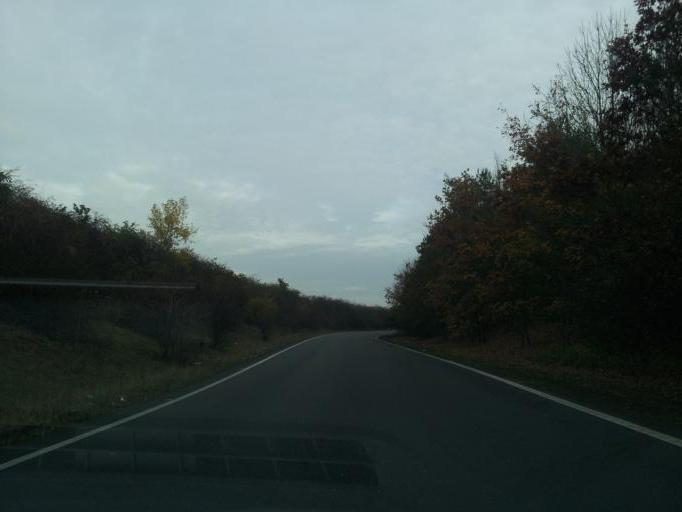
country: GB
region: England
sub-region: Cambridgeshire
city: Comberton
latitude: 52.2174
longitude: 0.0315
